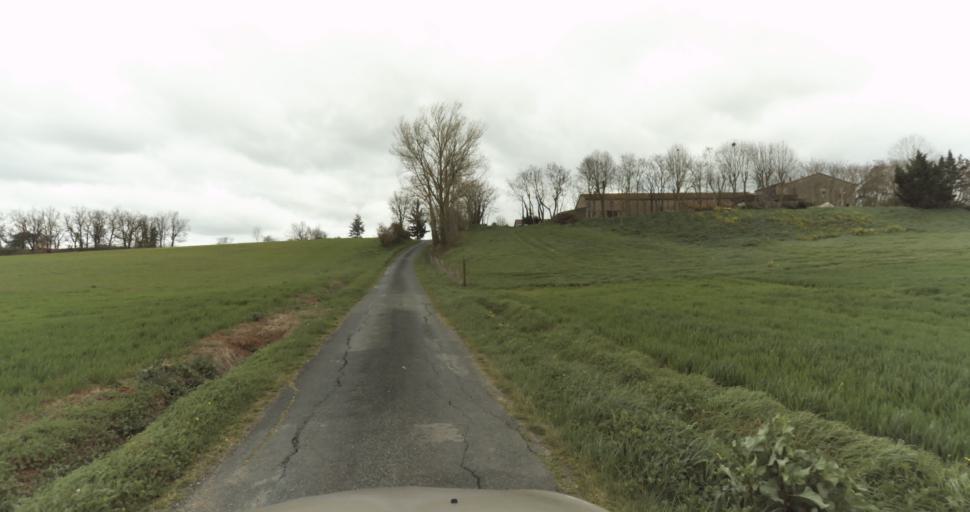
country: FR
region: Midi-Pyrenees
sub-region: Departement du Tarn
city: Puygouzon
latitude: 43.8727
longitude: 2.1774
